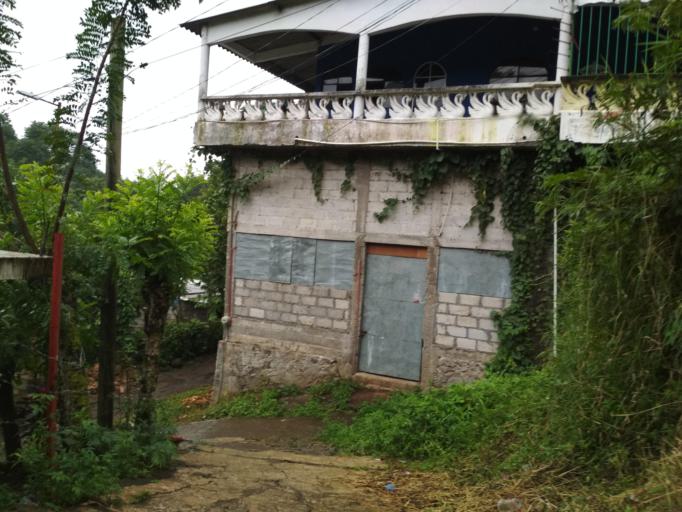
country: MX
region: Veracruz
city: San Andres Tuxtla
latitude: 18.4506
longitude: -95.1990
